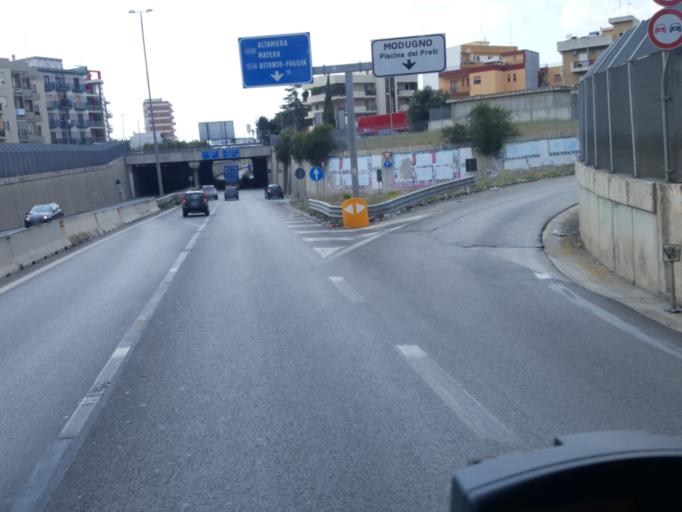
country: IT
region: Apulia
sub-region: Provincia di Bari
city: Modugno
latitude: 41.0887
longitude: 16.7797
